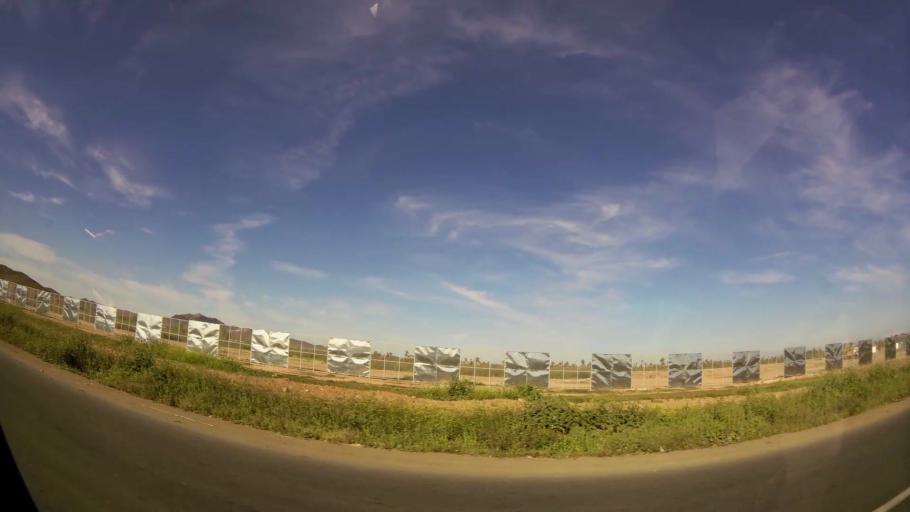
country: MA
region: Marrakech-Tensift-Al Haouz
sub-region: Marrakech
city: Marrakesh
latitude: 31.6957
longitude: -8.0580
